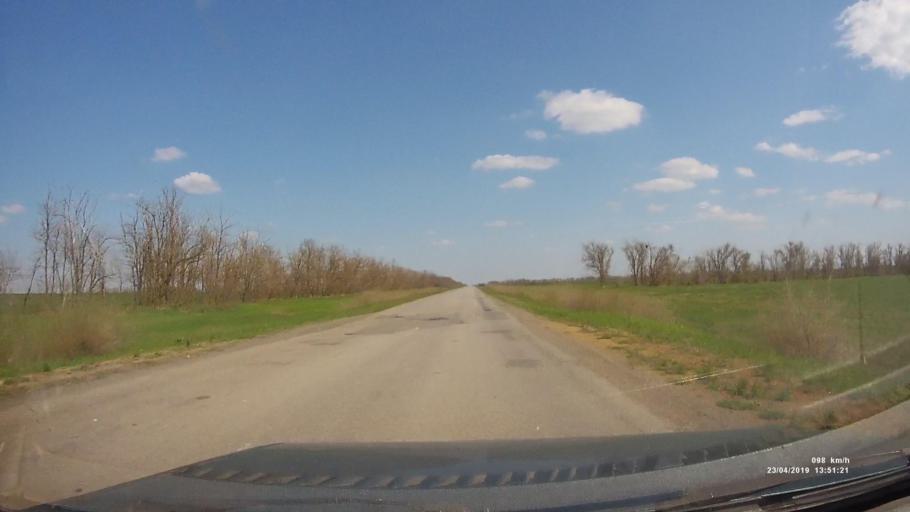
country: RU
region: Kalmykiya
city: Yashalta
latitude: 46.5995
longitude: 42.9323
